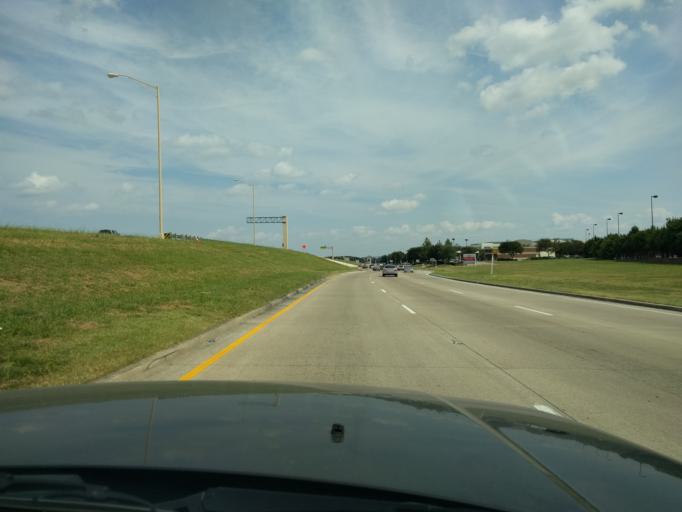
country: US
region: Texas
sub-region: Collin County
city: Plano
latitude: 33.0024
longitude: -96.6857
